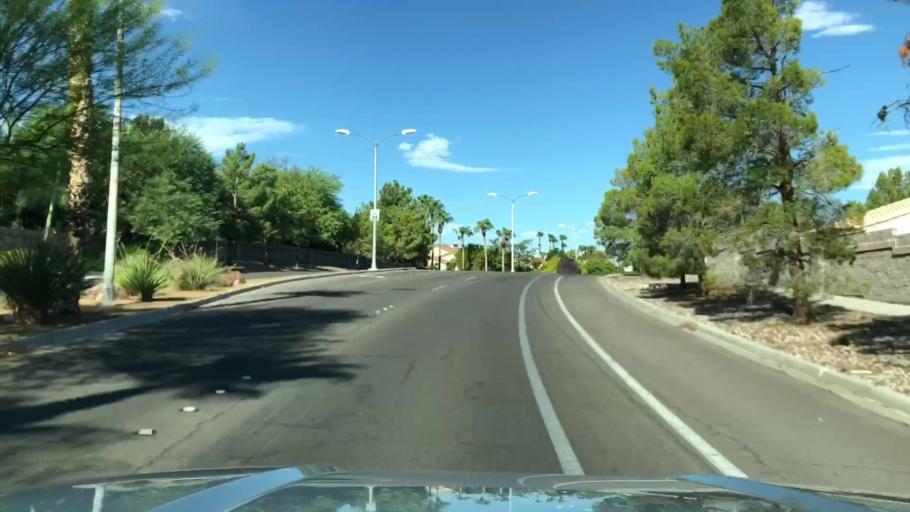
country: US
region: Nevada
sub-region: Clark County
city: Whitney
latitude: 36.0403
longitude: -115.0729
